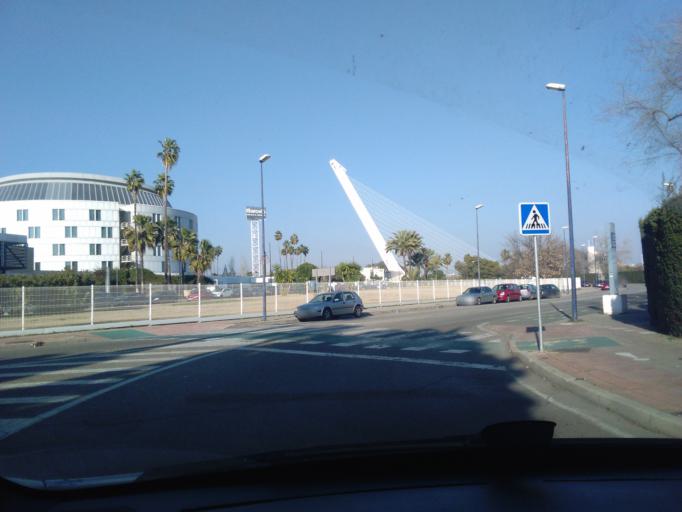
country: ES
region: Andalusia
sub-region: Provincia de Sevilla
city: Sevilla
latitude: 37.4089
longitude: -5.9958
